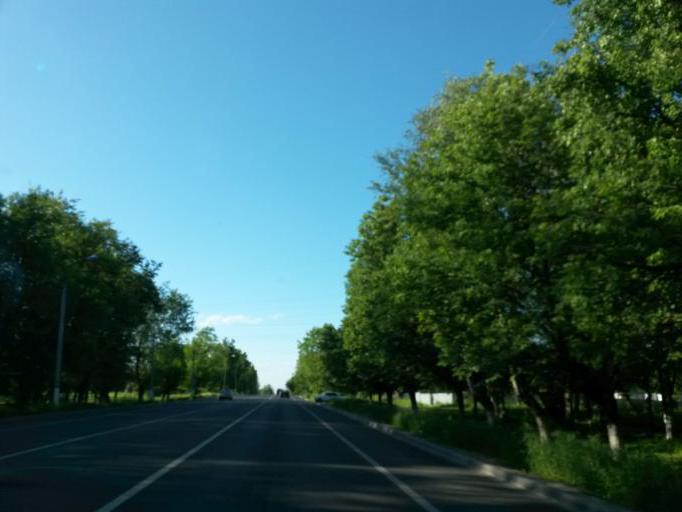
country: RU
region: Moskovskaya
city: L'vovskiy
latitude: 55.3194
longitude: 37.5287
